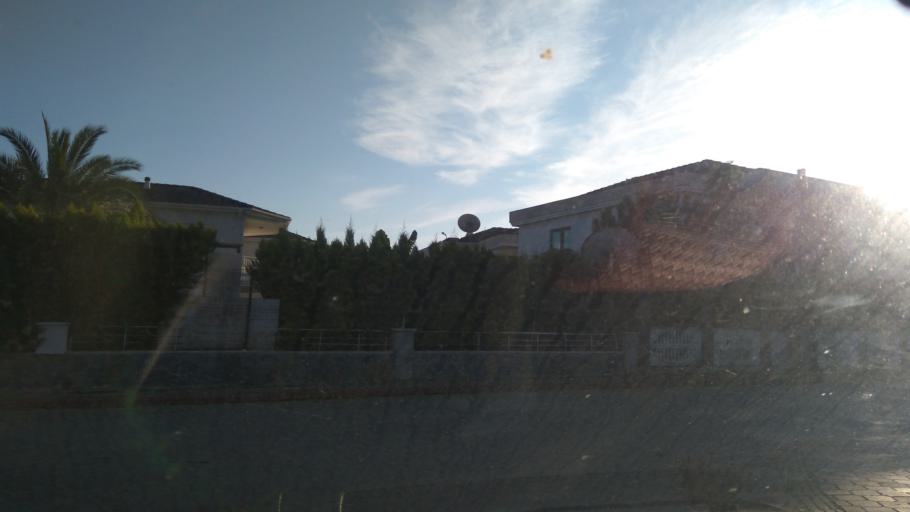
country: TR
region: Antalya
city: Kemer
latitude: 36.5657
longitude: 30.5601
